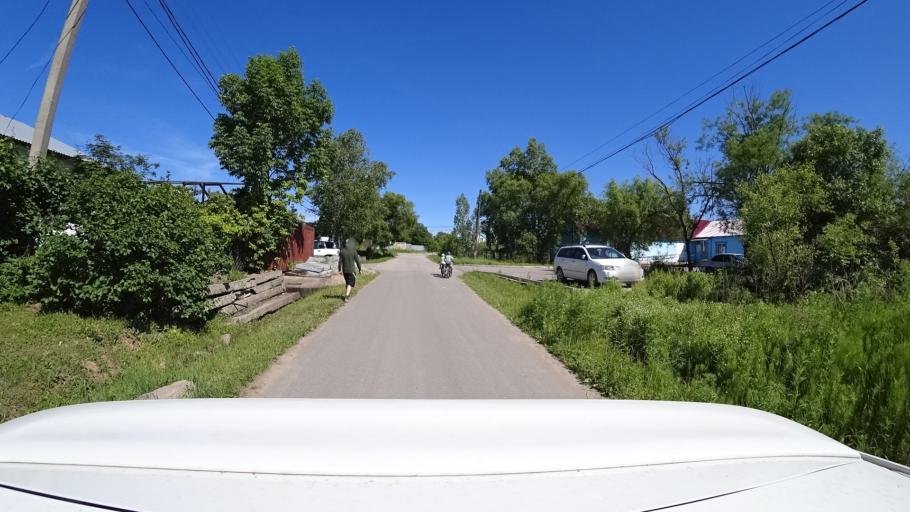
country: RU
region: Khabarovsk Krai
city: Topolevo
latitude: 48.5559
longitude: 135.1886
